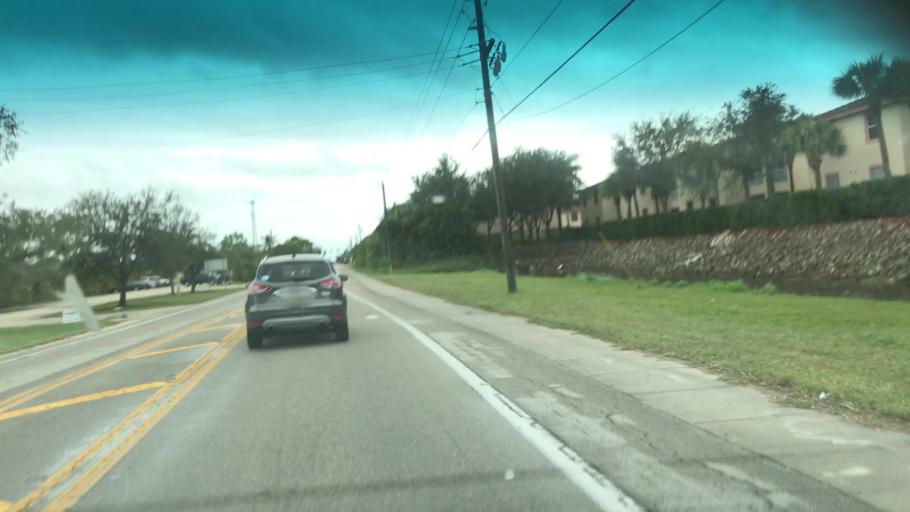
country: US
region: Florida
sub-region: Lee County
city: Harlem Heights
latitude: 26.5171
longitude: -81.9358
